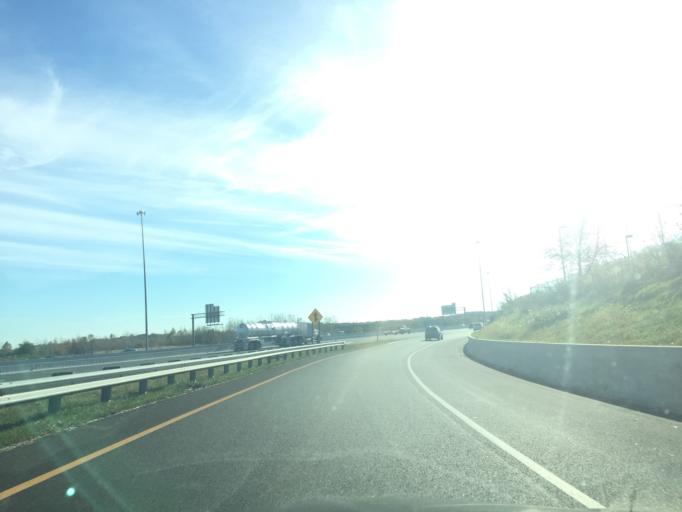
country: US
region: Maryland
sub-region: Baltimore County
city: White Marsh
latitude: 39.3769
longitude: -76.4526
